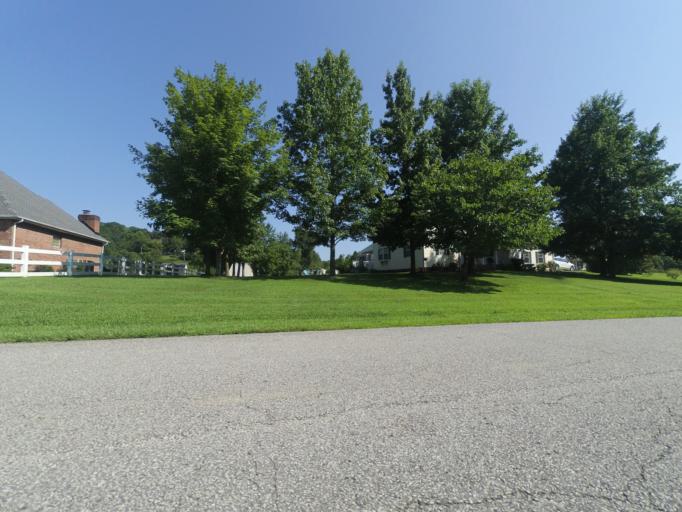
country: US
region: West Virginia
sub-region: Cabell County
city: Huntington
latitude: 38.4430
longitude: -82.4370
